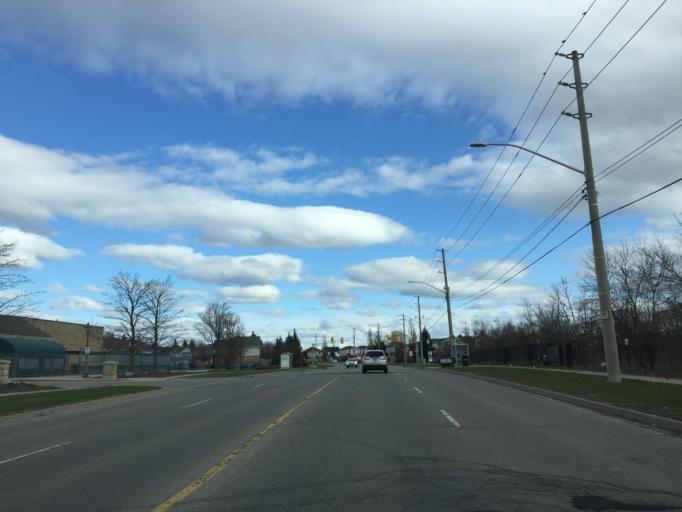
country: CA
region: Ontario
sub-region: Wellington County
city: Guelph
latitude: 43.5131
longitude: -80.2195
